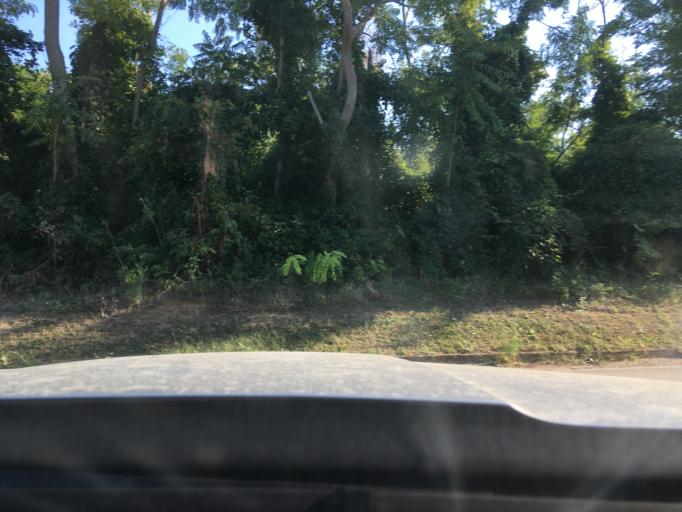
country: HR
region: Zadarska
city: Privlaka
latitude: 44.2481
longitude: 15.1481
